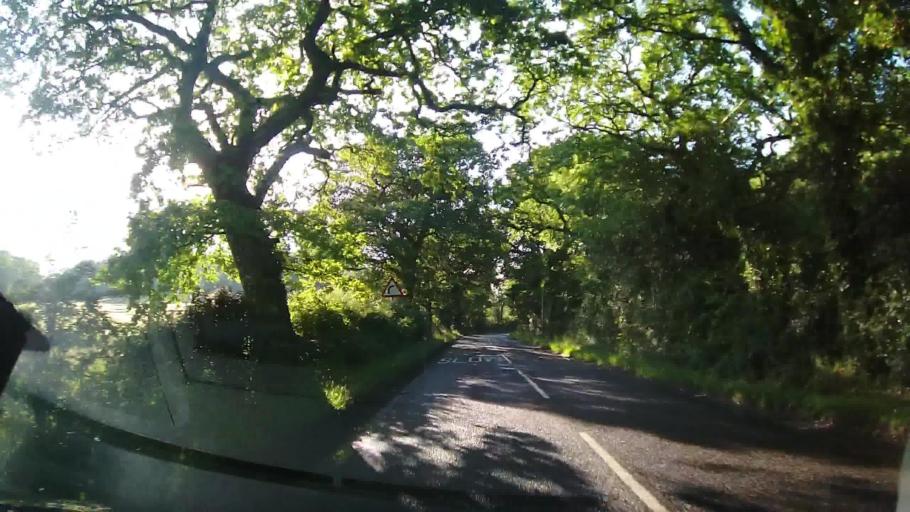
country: GB
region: England
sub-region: Leicestershire
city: Markfield
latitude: 52.6592
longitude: -1.2639
